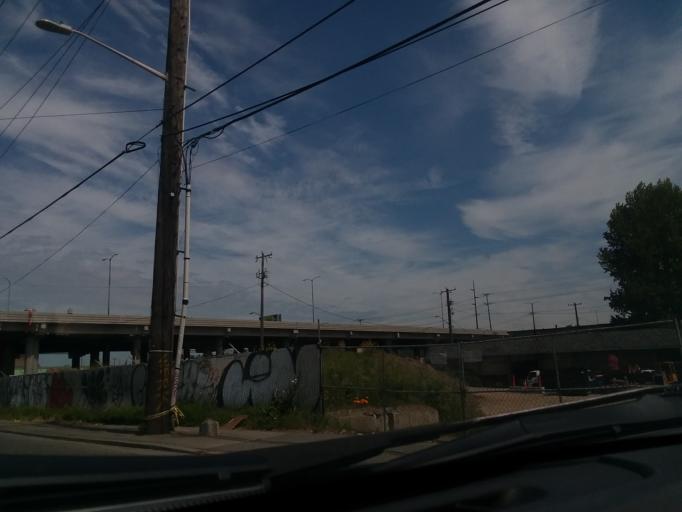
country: US
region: Washington
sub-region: King County
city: Seattle
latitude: 47.5709
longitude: -122.3341
